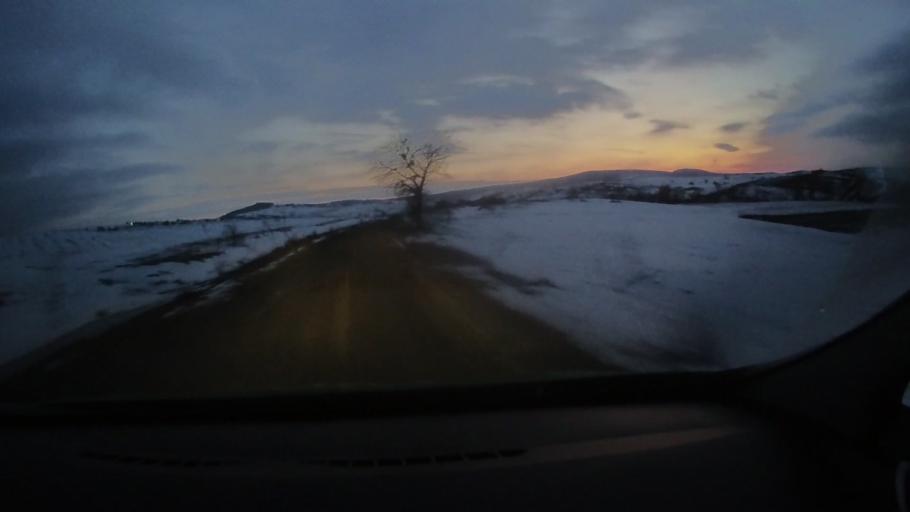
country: RO
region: Harghita
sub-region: Comuna Darjiu
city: Darjiu
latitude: 46.1624
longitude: 25.2097
